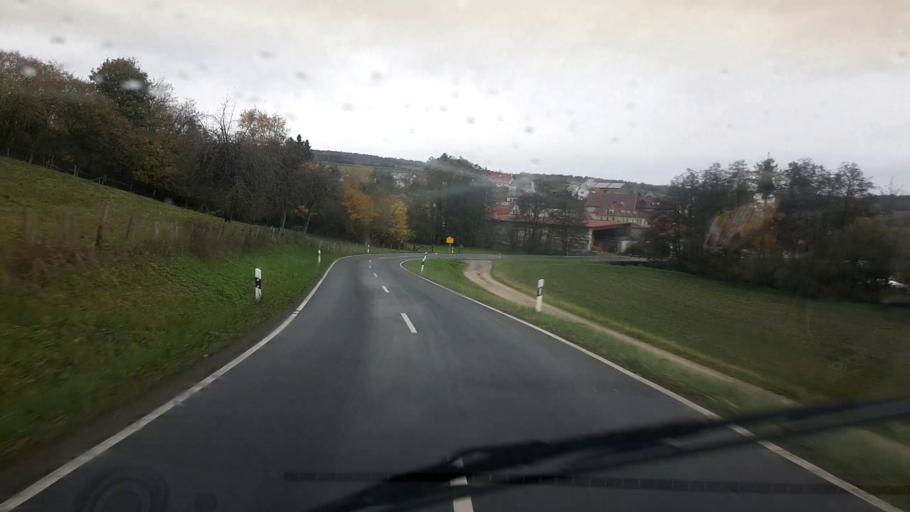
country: DE
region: Bavaria
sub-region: Upper Franconia
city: Burgwindheim
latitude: 49.8821
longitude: 10.5870
